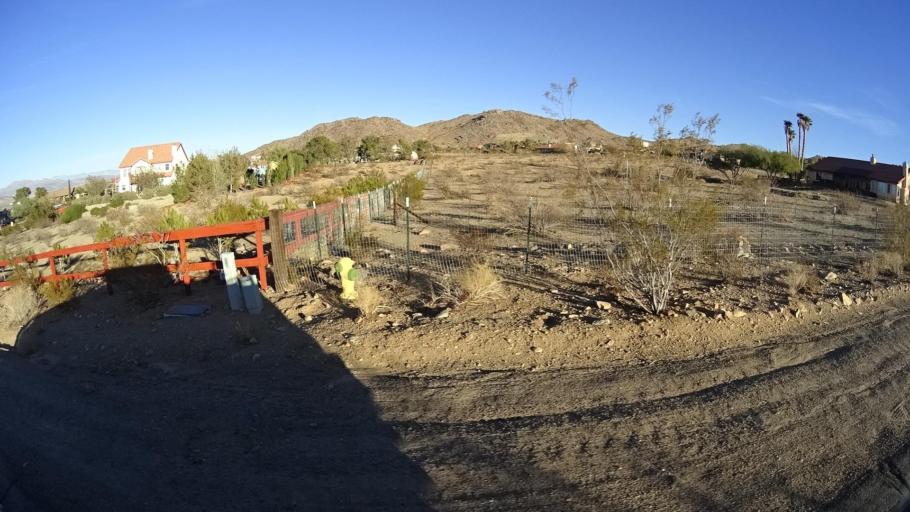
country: US
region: California
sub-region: Kern County
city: Ridgecrest
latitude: 35.5751
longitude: -117.6523
